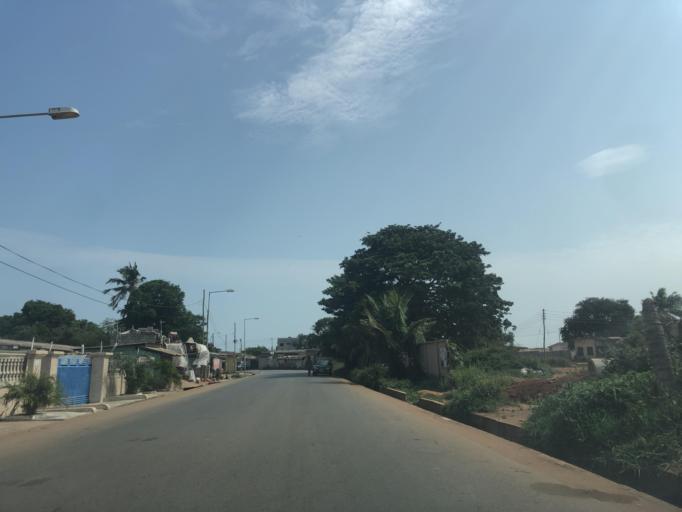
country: GH
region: Greater Accra
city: Accra
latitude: 5.5723
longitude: -0.1611
